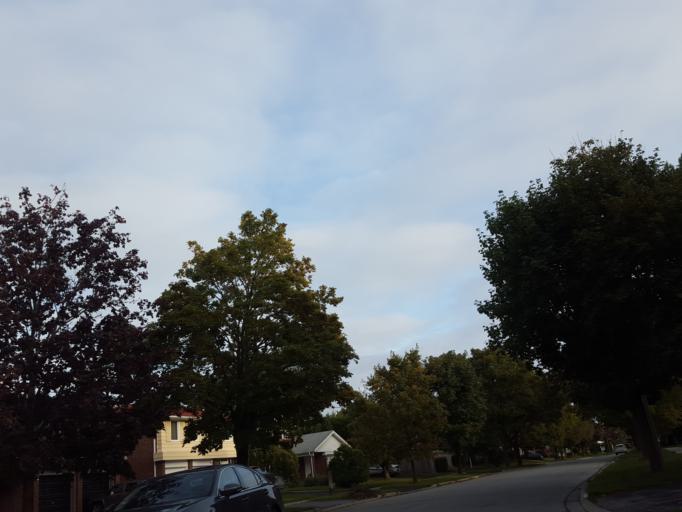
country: CA
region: Ontario
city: Scarborough
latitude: 43.7861
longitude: -79.3081
